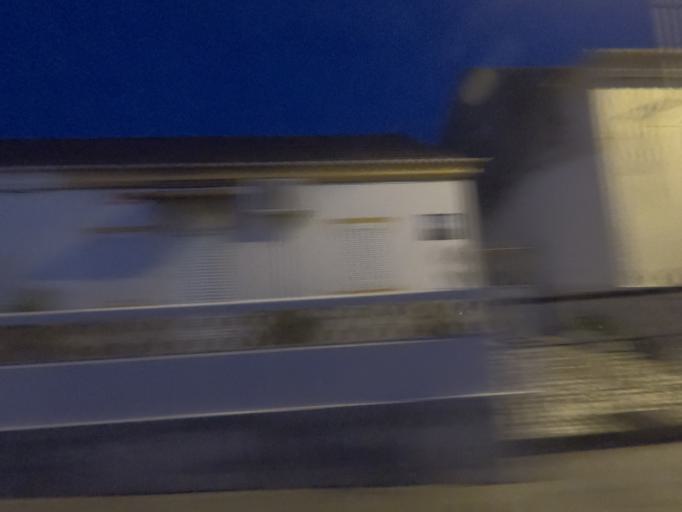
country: PT
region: Setubal
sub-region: Setubal
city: Setubal
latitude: 38.5346
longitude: -8.8994
